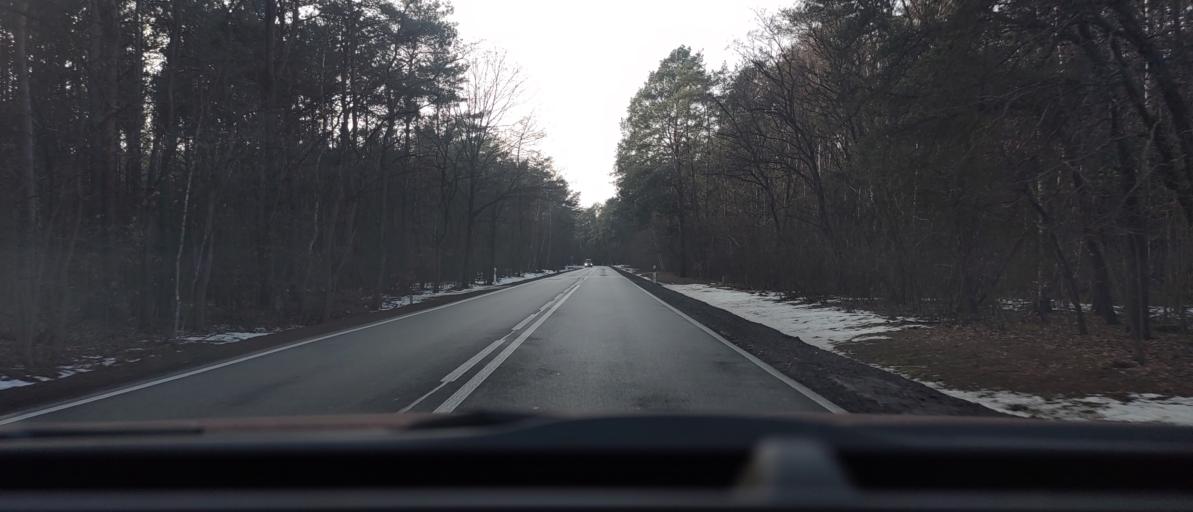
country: PL
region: Masovian Voivodeship
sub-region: Powiat bialobrzeski
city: Wysmierzyce
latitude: 51.6282
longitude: 20.8413
